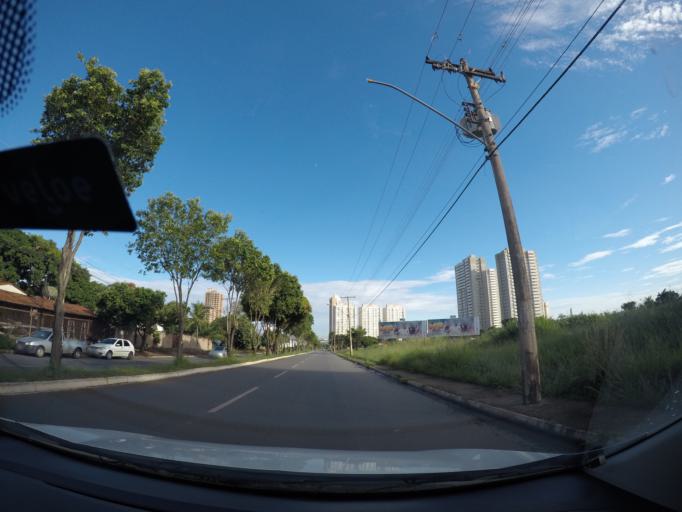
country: BR
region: Goias
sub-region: Goiania
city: Goiania
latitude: -16.7401
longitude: -49.2846
